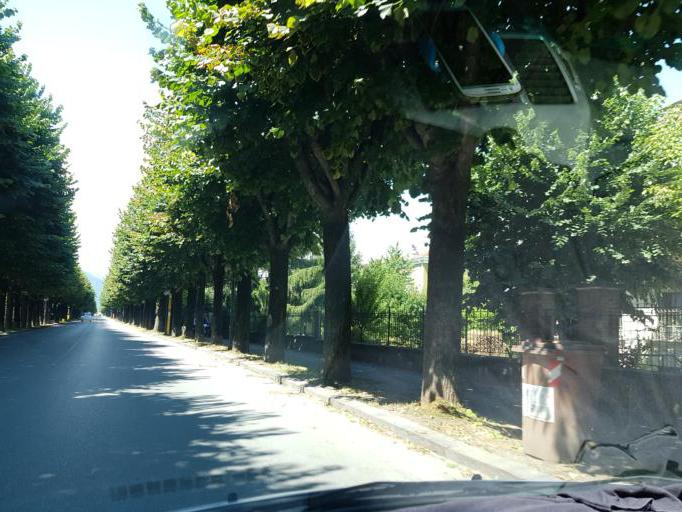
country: IT
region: Piedmont
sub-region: Provincia di Cuneo
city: Dronero
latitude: 44.4677
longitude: 7.3568
